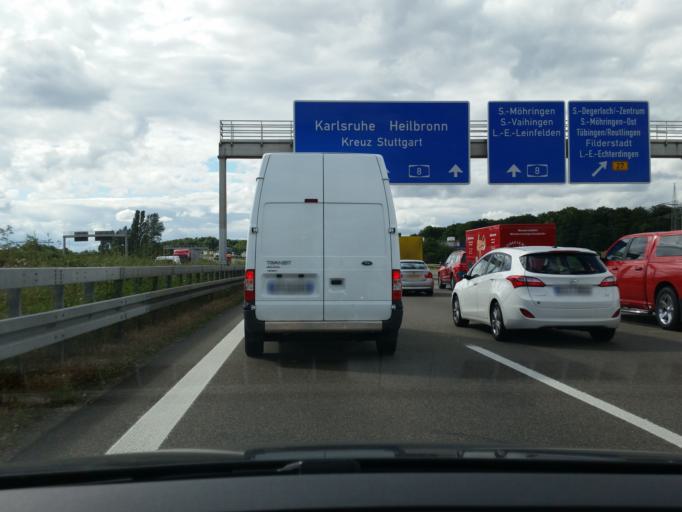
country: DE
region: Baden-Wuerttemberg
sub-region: Regierungsbezirk Stuttgart
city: Leinfelden-Echterdingen
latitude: 48.7026
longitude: 9.1777
